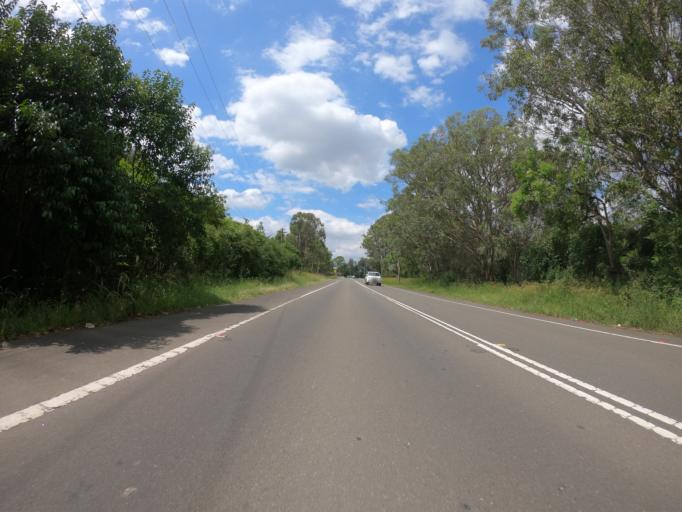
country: AU
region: New South Wales
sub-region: Blacktown
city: Mount Druitt
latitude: -33.8048
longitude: 150.7668
